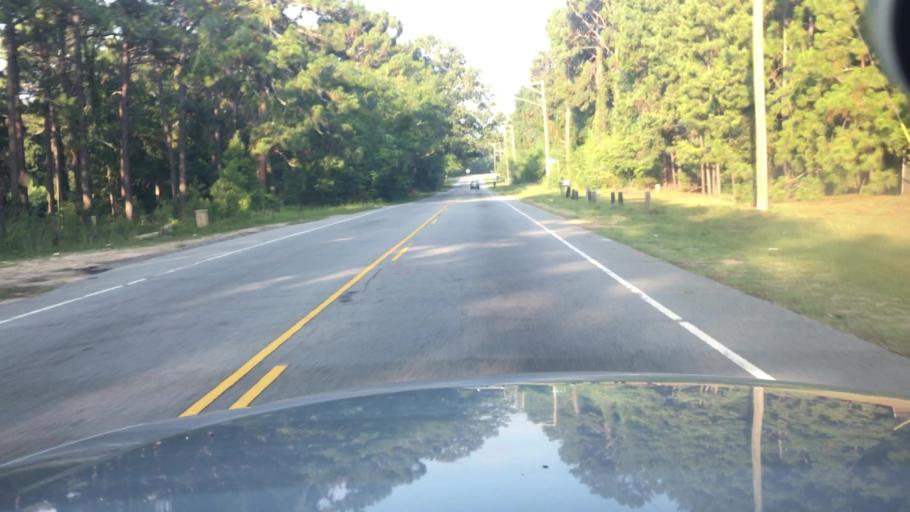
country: US
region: North Carolina
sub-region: Cumberland County
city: Spring Lake
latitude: 35.1060
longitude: -78.9458
